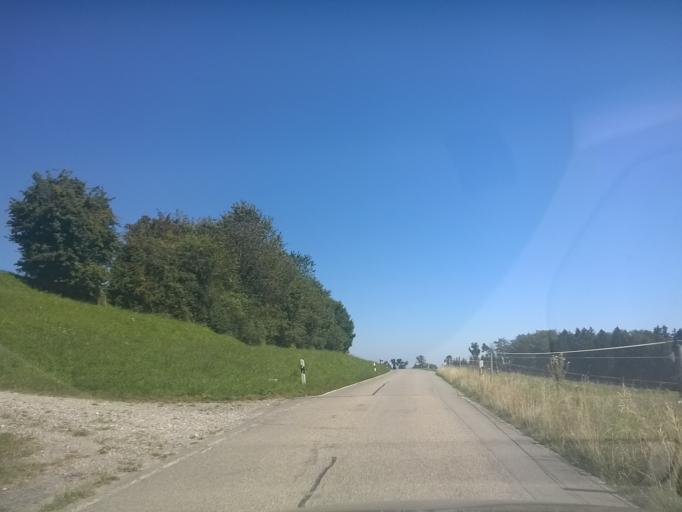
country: CH
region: Zurich
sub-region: Bezirk Winterthur
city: Brutten
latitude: 47.4887
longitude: 8.6591
